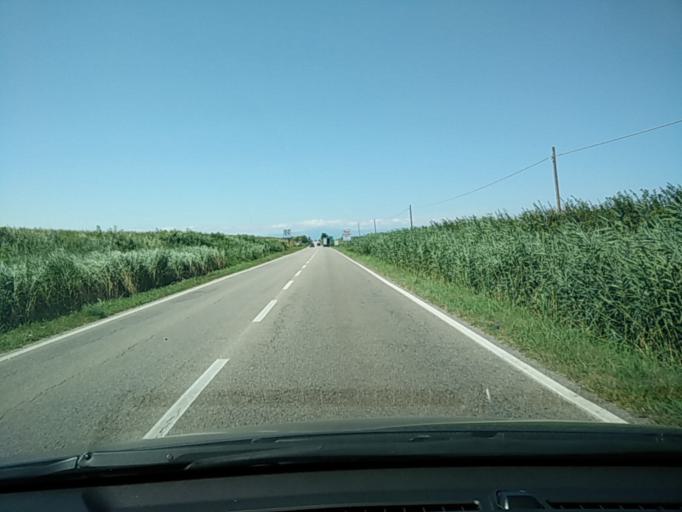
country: IT
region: Veneto
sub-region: Provincia di Venezia
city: Caorle
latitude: 45.6231
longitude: 12.8655
